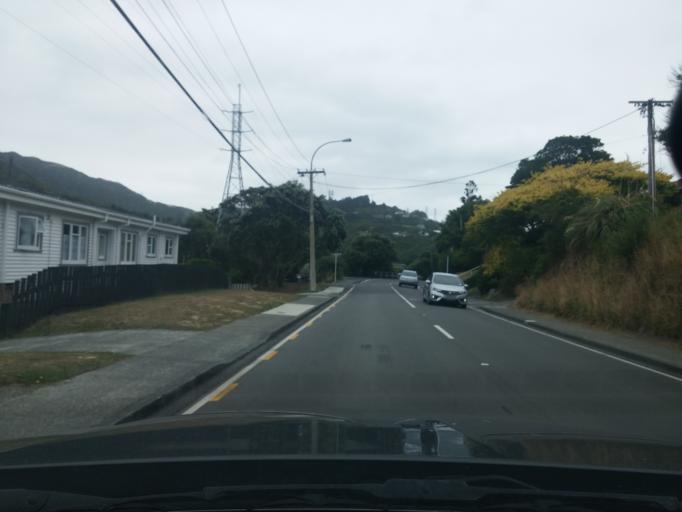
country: NZ
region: Wellington
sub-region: Wellington City
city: Kelburn
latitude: -41.2696
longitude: 174.7550
